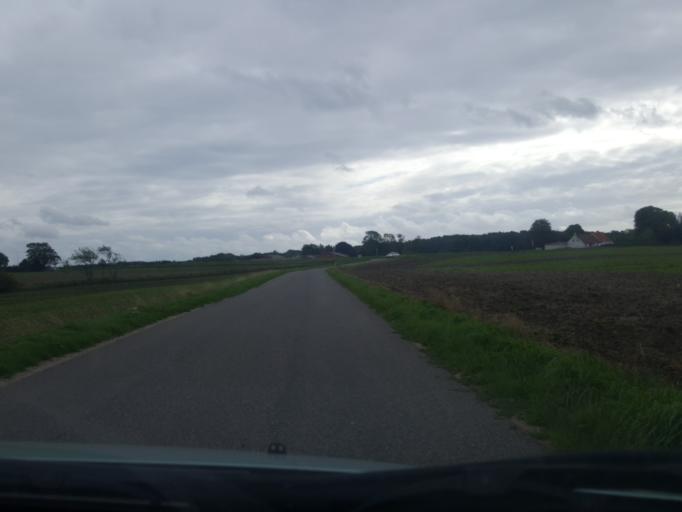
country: DK
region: Zealand
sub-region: Soro Kommune
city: Soro
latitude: 55.4632
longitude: 11.5187
